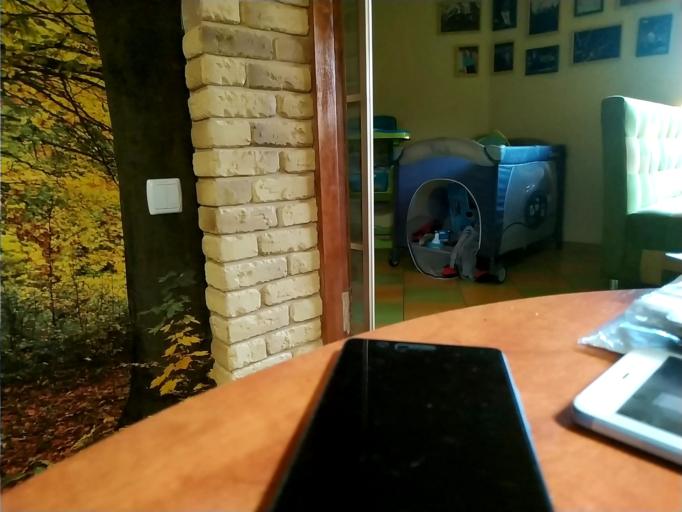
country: RU
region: Kaluga
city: Seredeyskiy
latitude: 53.7702
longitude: 35.4047
